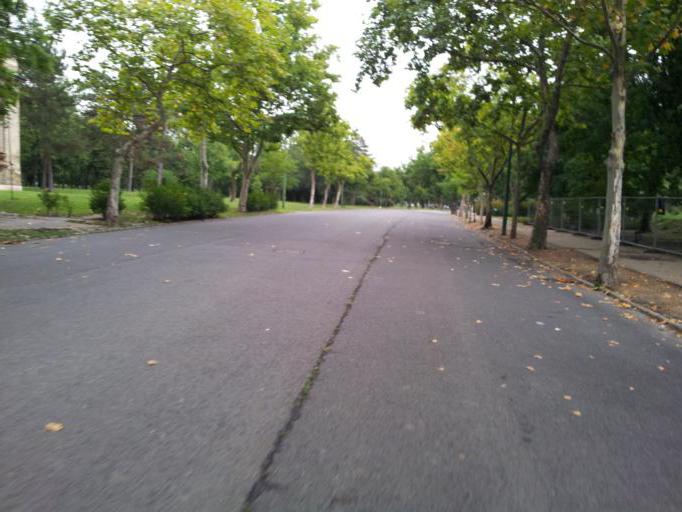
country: HU
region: Budapest
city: Budapest XIII. keruelet
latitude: 47.5119
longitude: 19.0873
